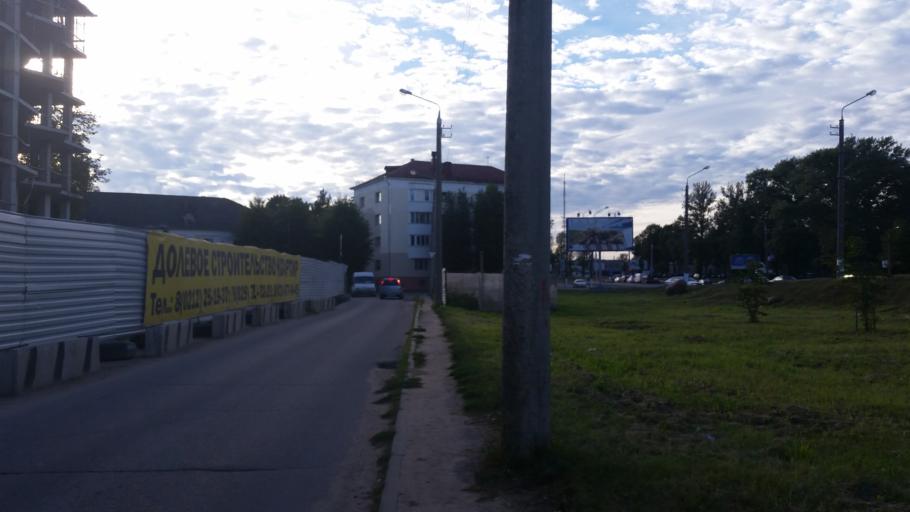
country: BY
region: Vitebsk
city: Vitebsk
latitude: 55.1844
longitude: 30.1927
